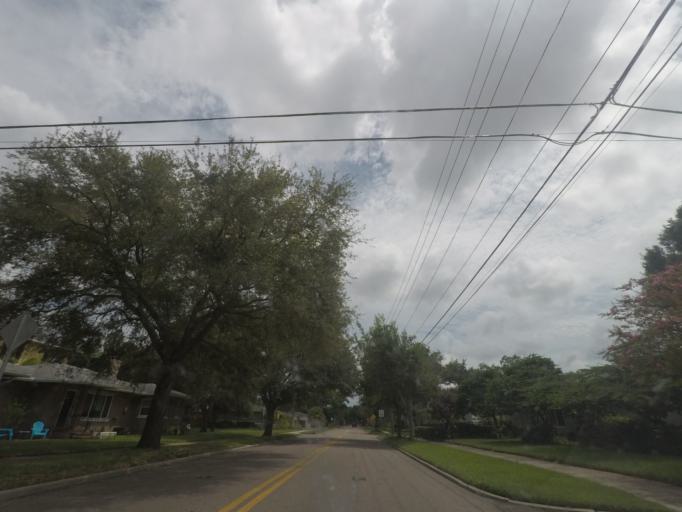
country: US
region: Florida
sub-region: Pinellas County
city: Lealman
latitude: 27.7972
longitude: -82.6345
